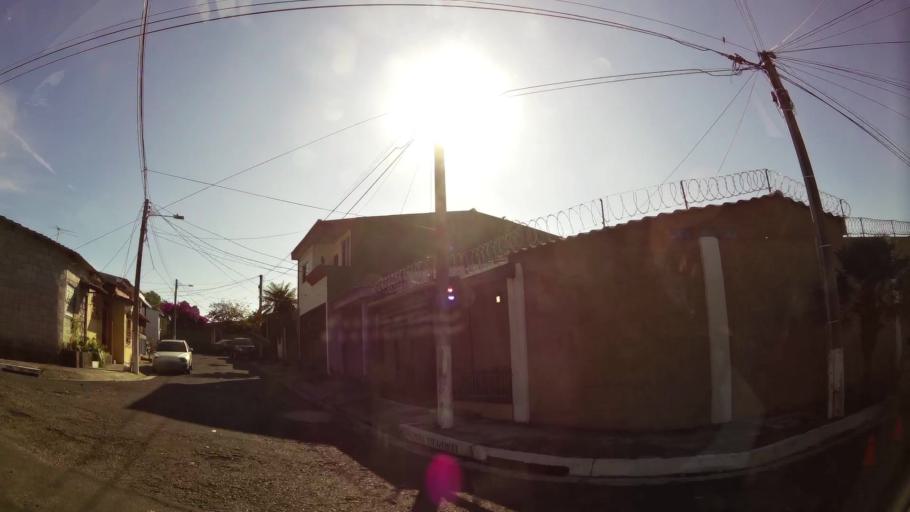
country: SV
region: La Libertad
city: Santa Tecla
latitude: 13.6919
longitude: -89.2924
